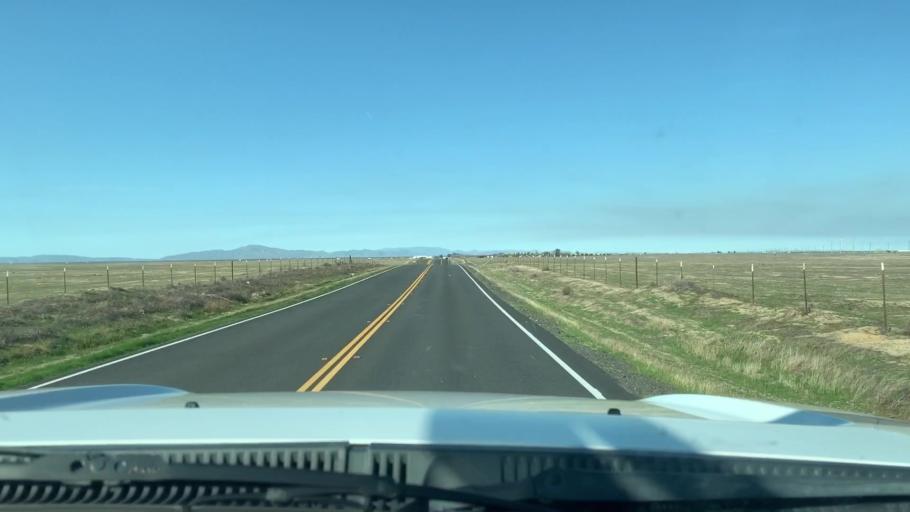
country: US
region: California
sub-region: Kern County
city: Lost Hills
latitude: 35.5953
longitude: -119.8436
